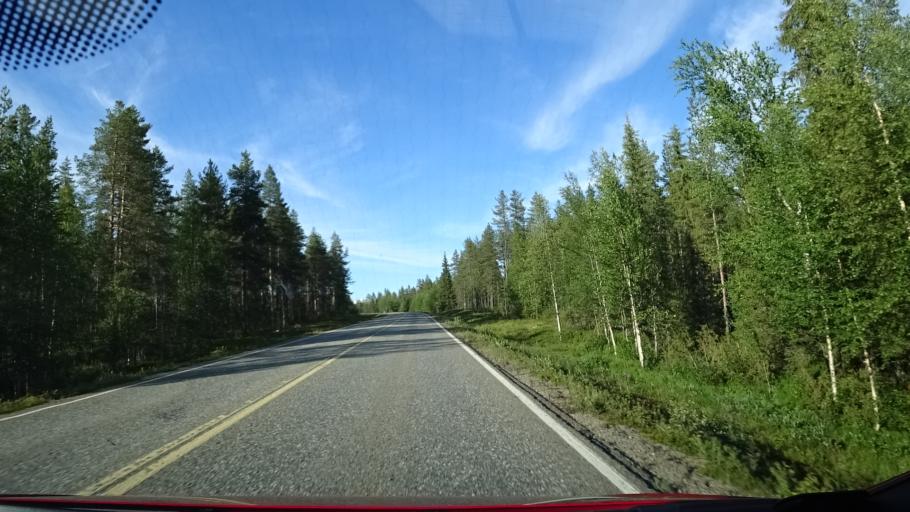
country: FI
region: Lapland
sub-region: Pohjois-Lappi
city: Sodankylae
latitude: 67.8427
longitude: 26.7246
